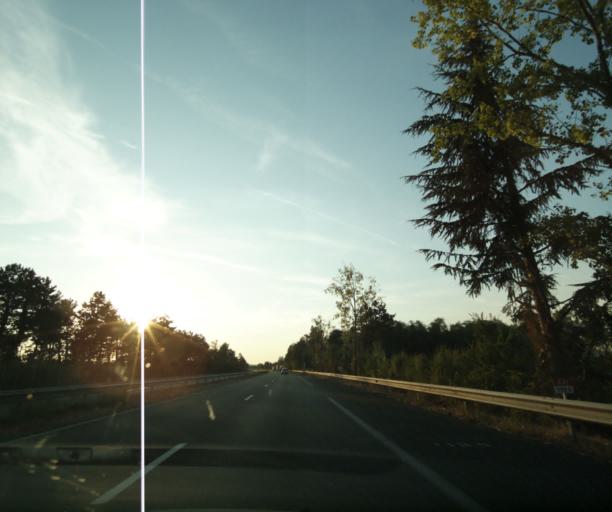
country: FR
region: Aquitaine
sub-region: Departement du Lot-et-Garonne
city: Roquefort
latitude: 44.1837
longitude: 0.5565
